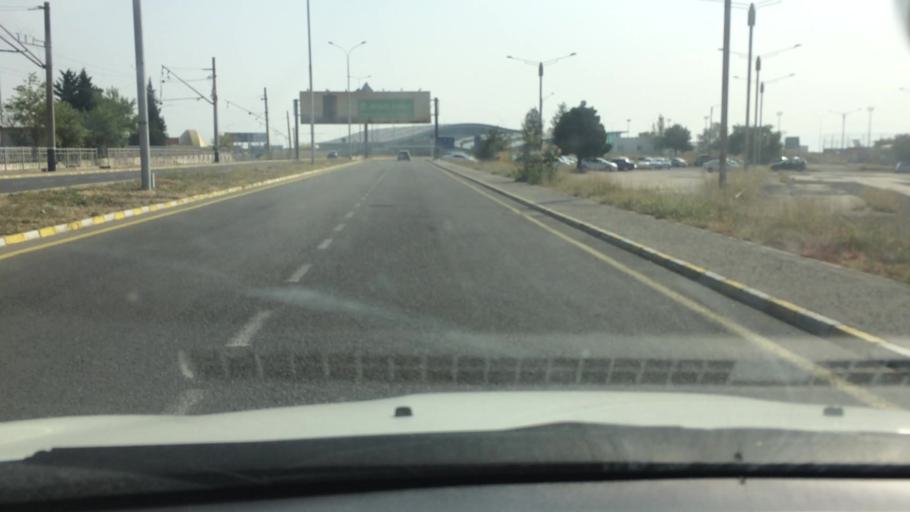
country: GE
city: Didi Lilo
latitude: 41.6739
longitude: 44.9619
